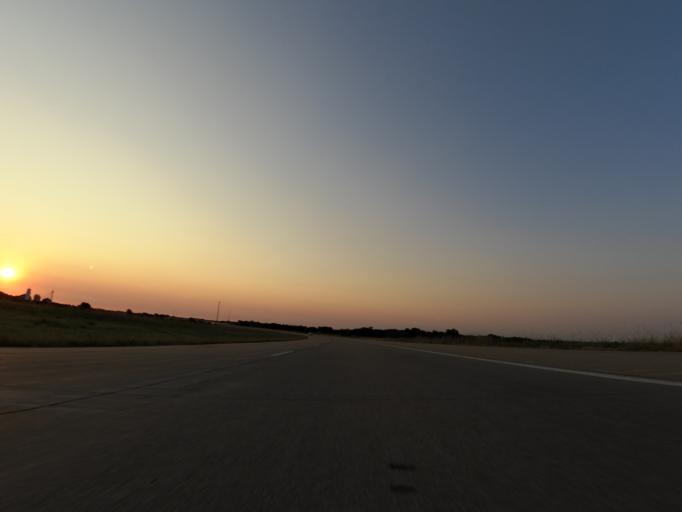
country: US
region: Kansas
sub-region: Reno County
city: Haven
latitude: 37.9383
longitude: -97.8787
